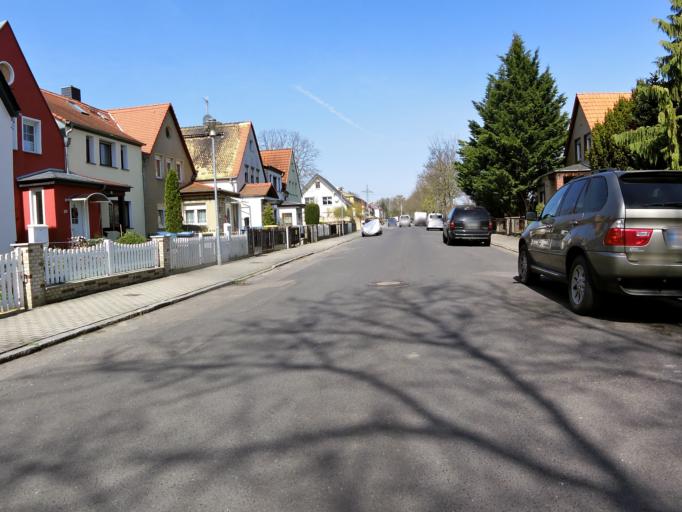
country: DE
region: Saxony
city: Schkeuditz
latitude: 51.3874
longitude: 12.2830
